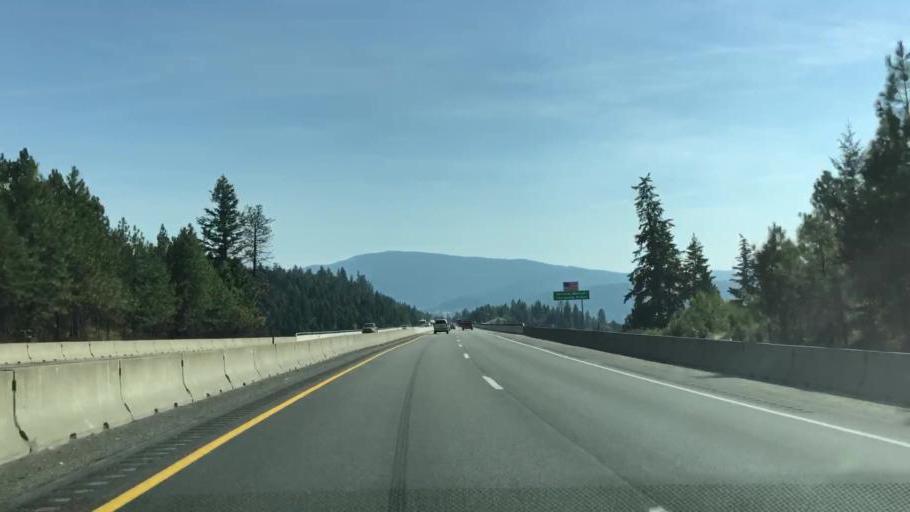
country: US
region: Idaho
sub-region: Kootenai County
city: Coeur d'Alene
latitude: 47.6504
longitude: -116.7152
